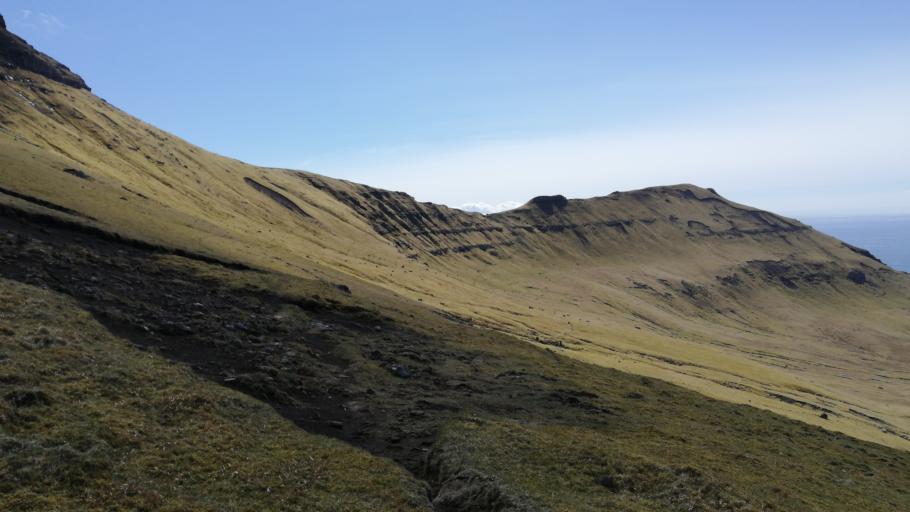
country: FO
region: Streymoy
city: Kollafjordhur
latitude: 62.0680
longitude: -6.9804
